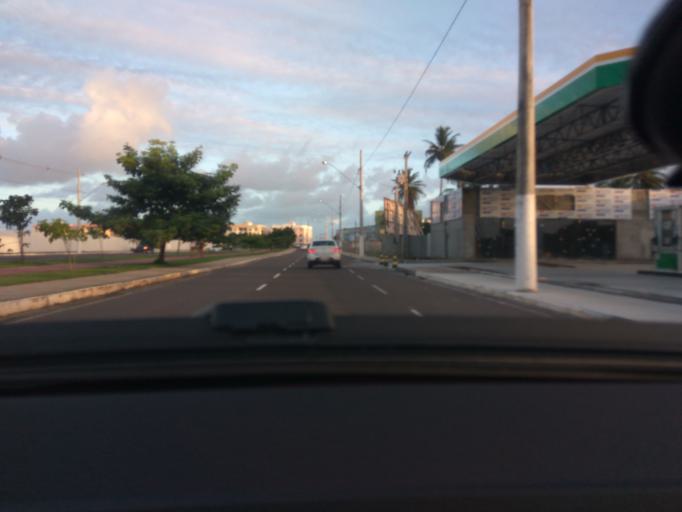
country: BR
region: Sergipe
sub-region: Aracaju
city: Aracaju
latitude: -10.9635
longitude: -37.0691
